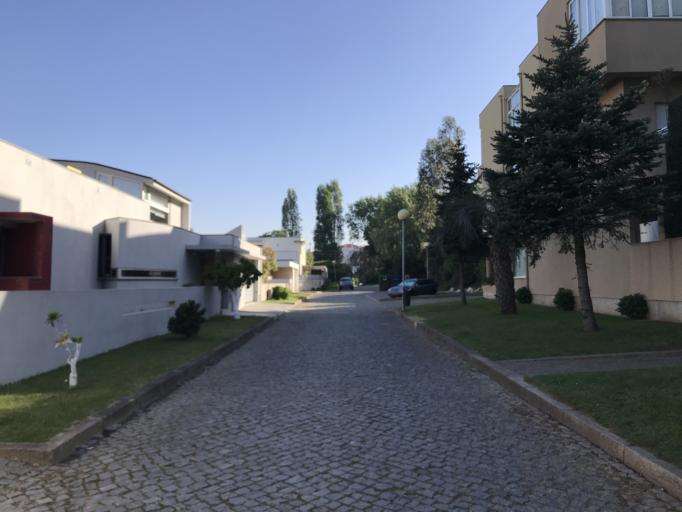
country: PT
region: Porto
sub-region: Matosinhos
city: Senhora da Hora
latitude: 41.1791
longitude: -8.6675
